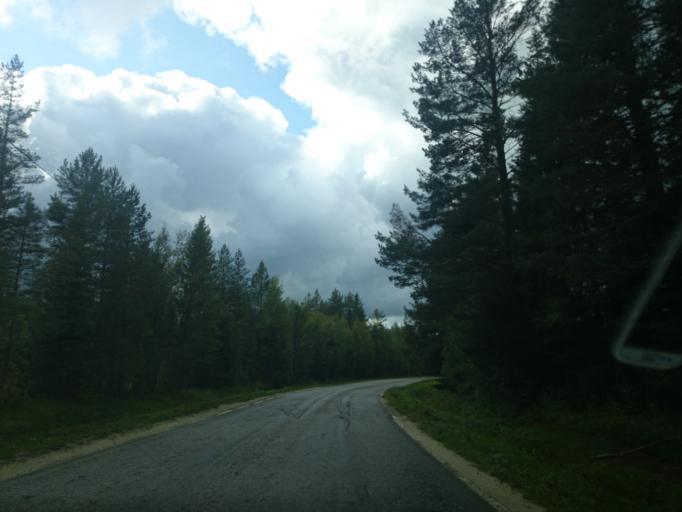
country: SE
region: Jaemtland
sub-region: Bergs Kommun
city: Hoverberg
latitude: 62.4649
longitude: 14.4953
